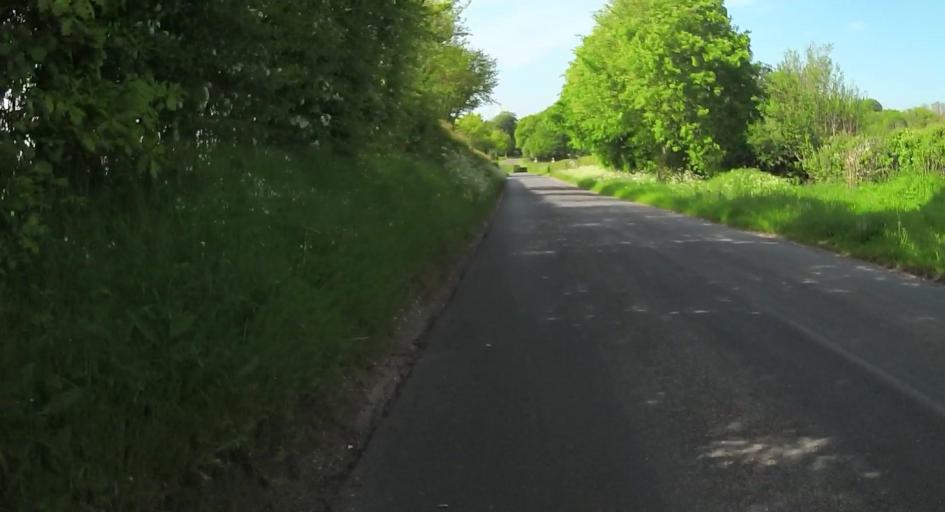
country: GB
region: England
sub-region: Hampshire
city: Four Marks
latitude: 51.1341
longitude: -1.0663
